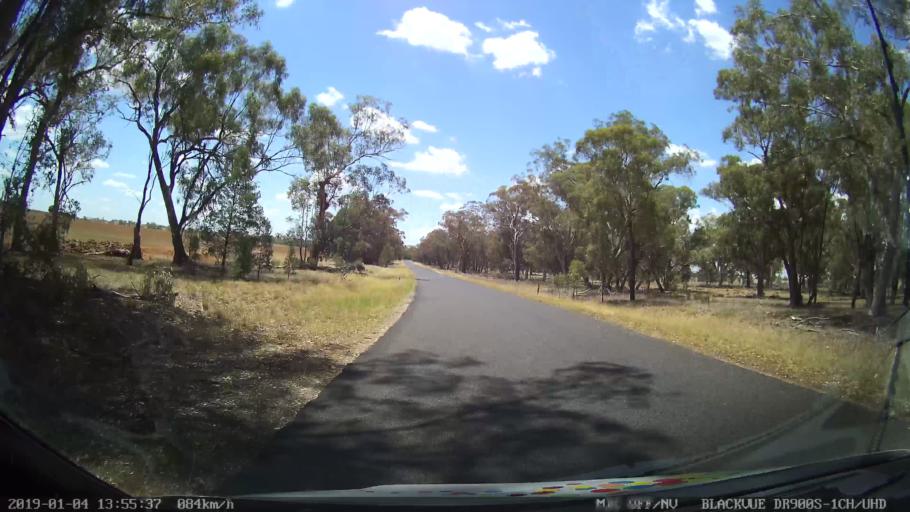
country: AU
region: New South Wales
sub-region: Dubbo Municipality
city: Dubbo
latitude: -32.3604
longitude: 148.5890
